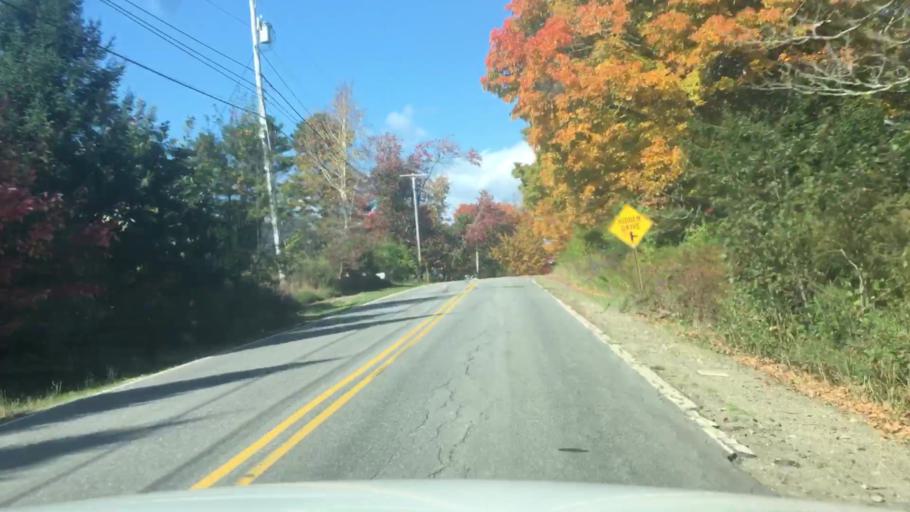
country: US
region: Maine
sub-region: Knox County
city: Warren
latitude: 44.0921
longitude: -69.2164
